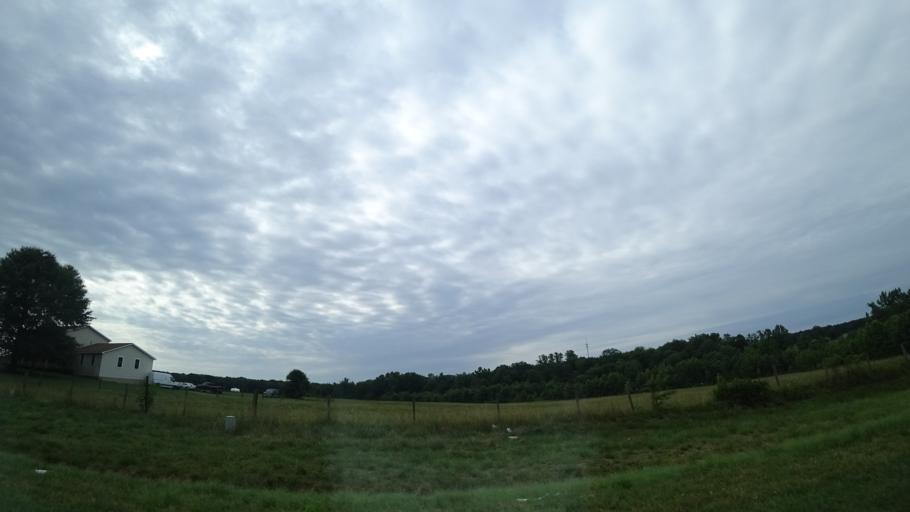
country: US
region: Virginia
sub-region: Spotsylvania County
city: Spotsylvania Courthouse
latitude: 38.1489
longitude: -77.6958
